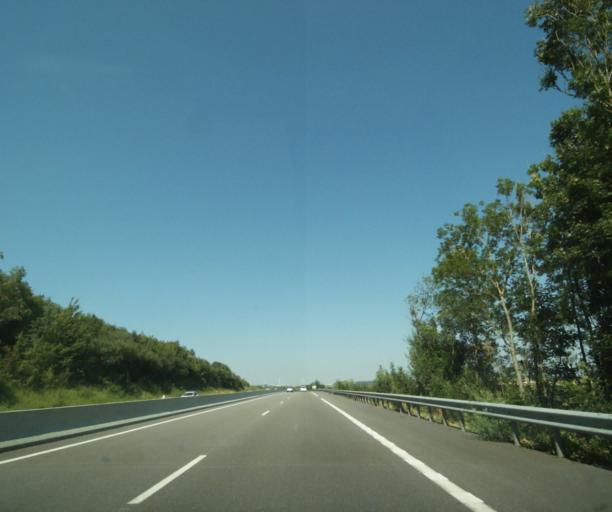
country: FR
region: Lorraine
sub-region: Departement de la Meuse
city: Lerouville
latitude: 48.7065
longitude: 5.4901
